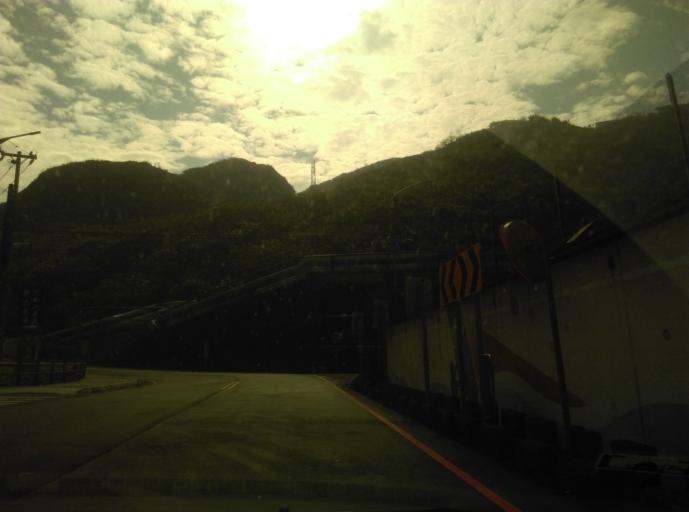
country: TW
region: Taiwan
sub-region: Keelung
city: Keelung
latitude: 25.1604
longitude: 121.7321
